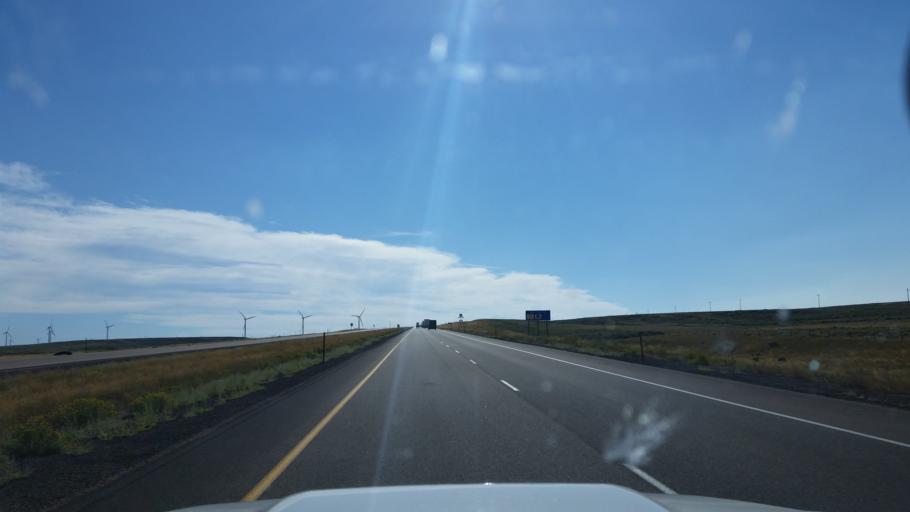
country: US
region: Wyoming
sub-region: Uinta County
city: Mountain View
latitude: 41.3184
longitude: -110.4916
